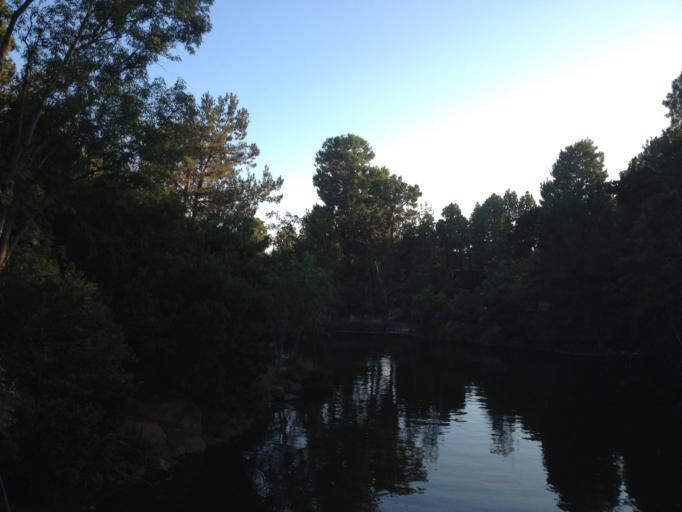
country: US
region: California
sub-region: Orange County
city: Anaheim
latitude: 33.8135
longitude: -117.9213
